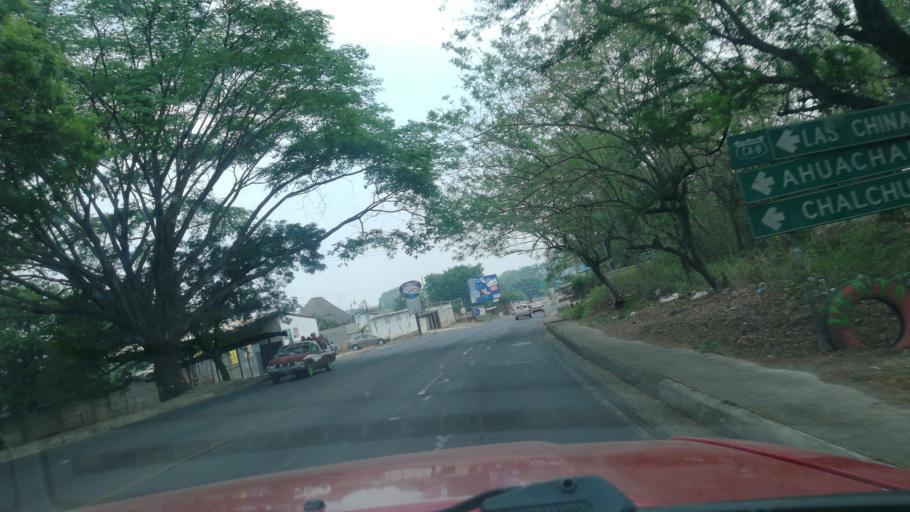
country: SV
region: Santa Ana
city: Santa Ana
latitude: 13.9813
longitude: -89.5961
